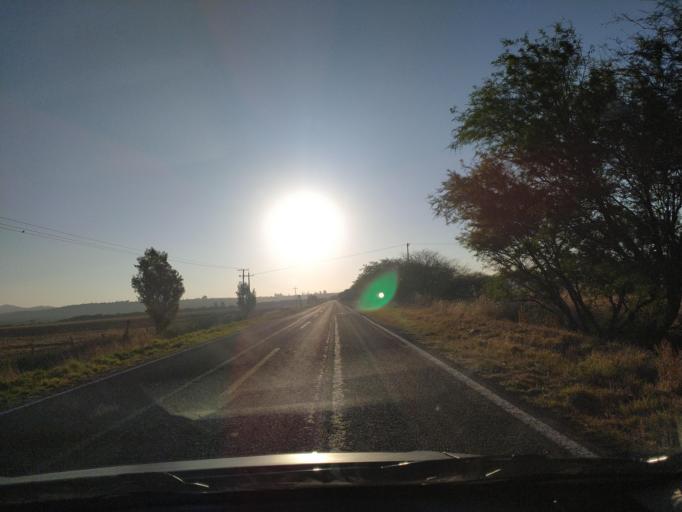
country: MX
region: Guanajuato
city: Ciudad Manuel Doblado
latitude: 20.7355
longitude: -101.8434
